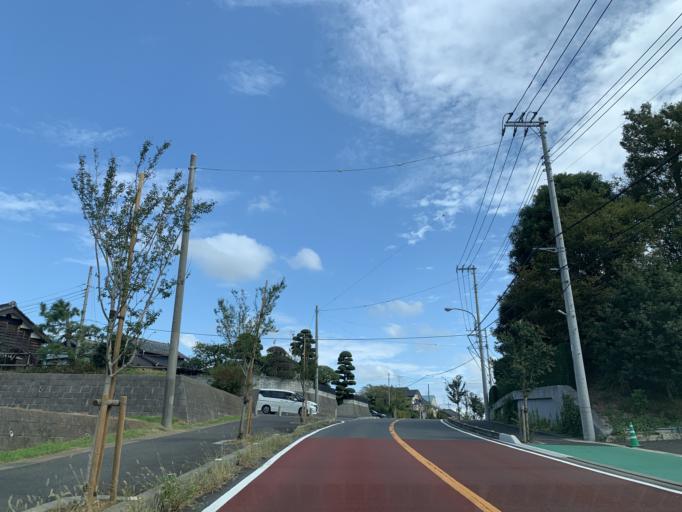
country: JP
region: Chiba
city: Nagareyama
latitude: 35.8510
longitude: 139.9086
